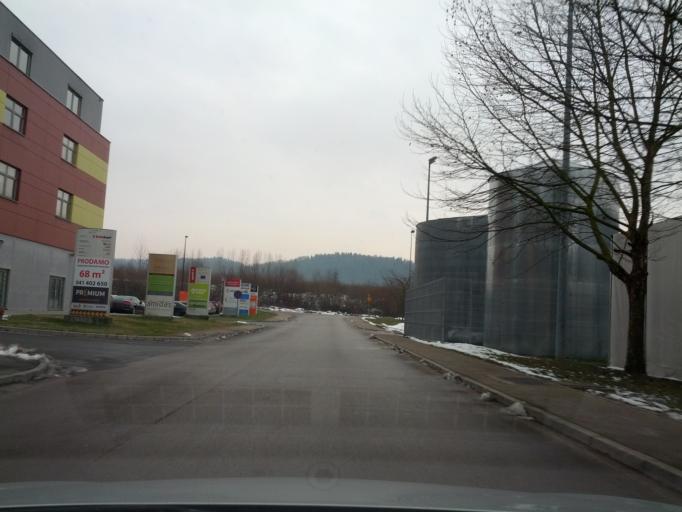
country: SI
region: Skofljica
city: Lavrica
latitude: 46.0213
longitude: 14.5385
